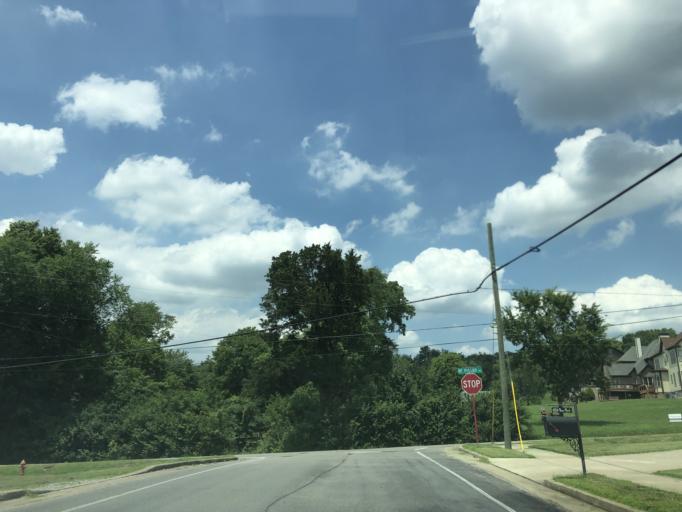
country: US
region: Tennessee
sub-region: Williamson County
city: Brentwood Estates
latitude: 36.0202
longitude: -86.7306
